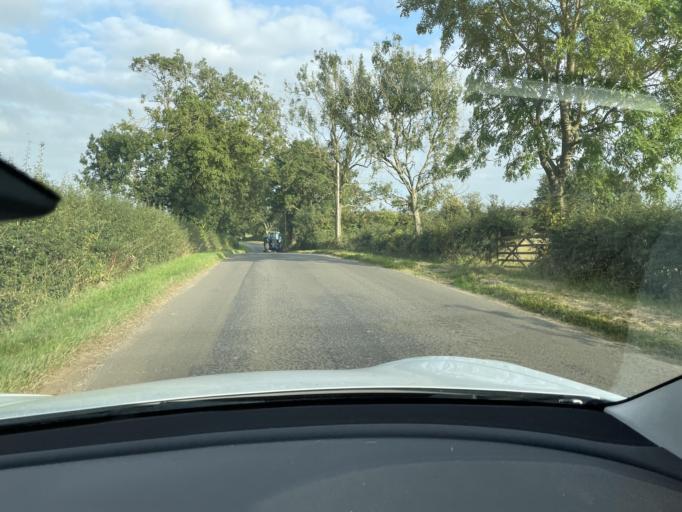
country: GB
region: England
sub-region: Northamptonshire
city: Brixworth
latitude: 52.3918
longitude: -0.9632
